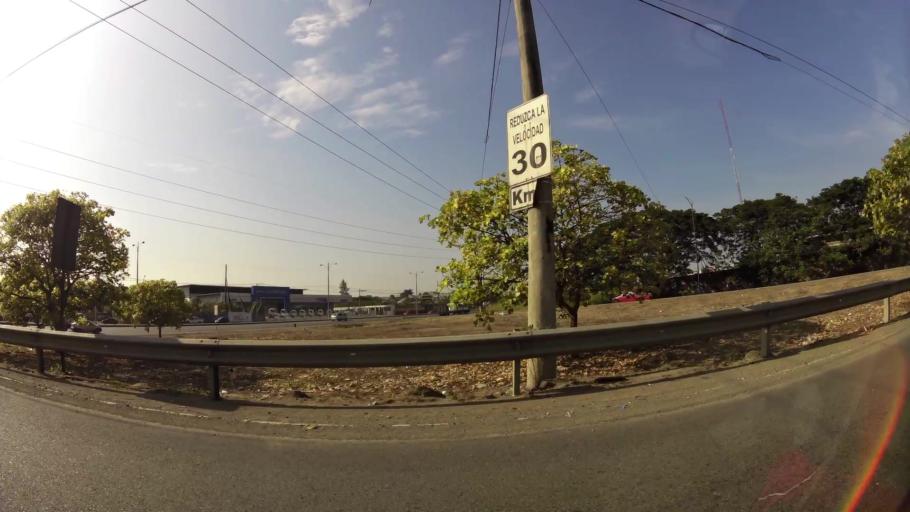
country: EC
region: Guayas
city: Santa Lucia
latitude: -2.0842
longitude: -79.9392
